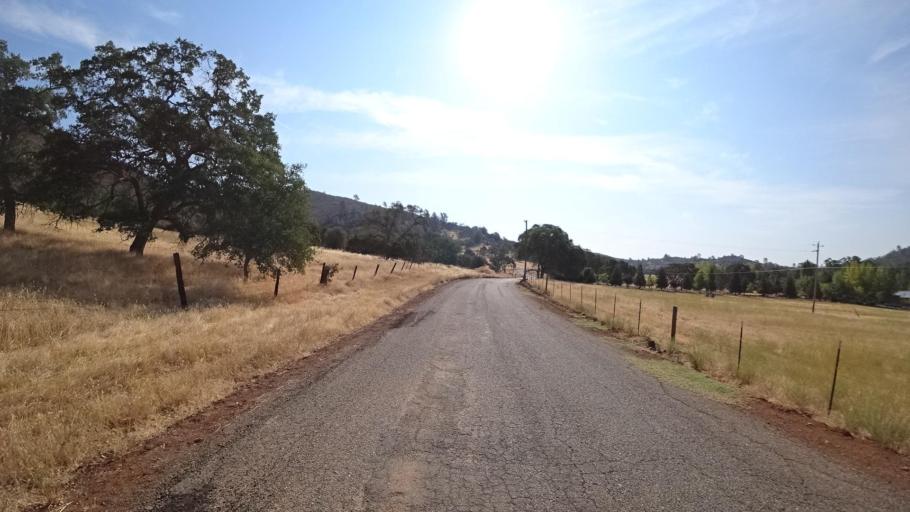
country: US
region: California
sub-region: Tuolumne County
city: Tuolumne City
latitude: 37.7225
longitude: -120.2856
